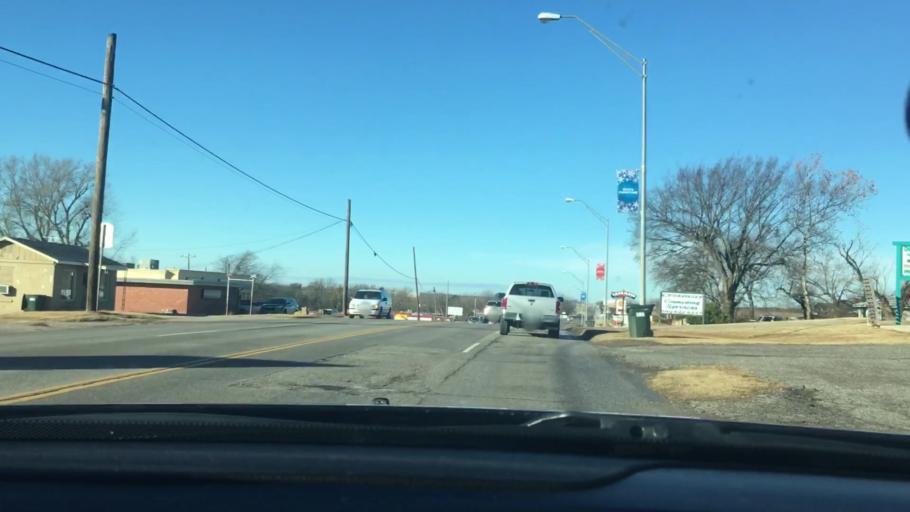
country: US
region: Oklahoma
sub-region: Murray County
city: Sulphur
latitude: 34.5065
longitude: -96.9900
